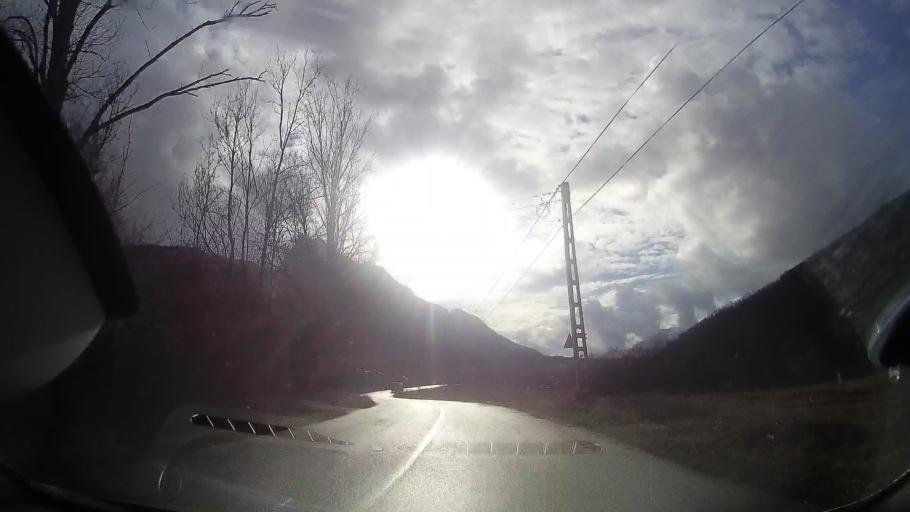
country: RO
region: Alba
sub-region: Comuna Rimetea
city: Rimetea
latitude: 46.4738
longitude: 23.5846
